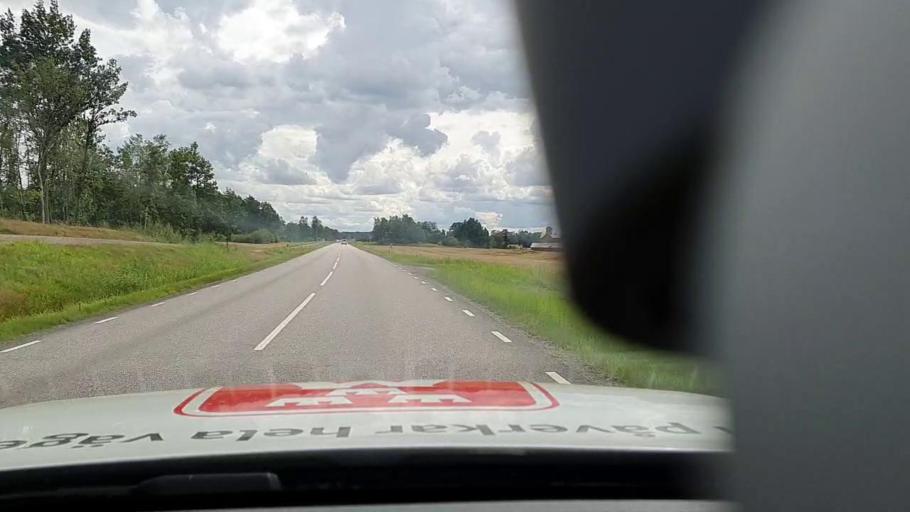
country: SE
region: Vaestra Goetaland
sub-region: Lidkopings Kommun
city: Lidkoping
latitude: 58.5541
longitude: 13.1162
